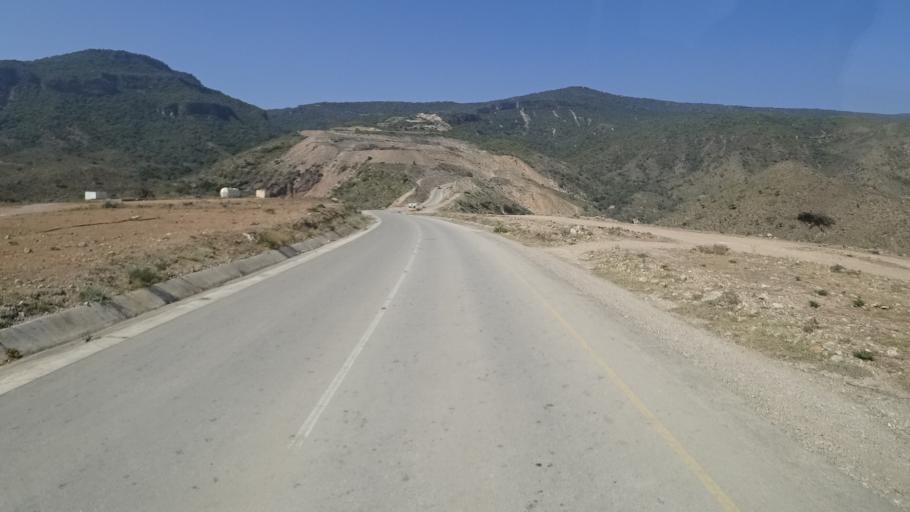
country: OM
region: Zufar
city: Salalah
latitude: 17.0397
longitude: 54.6130
